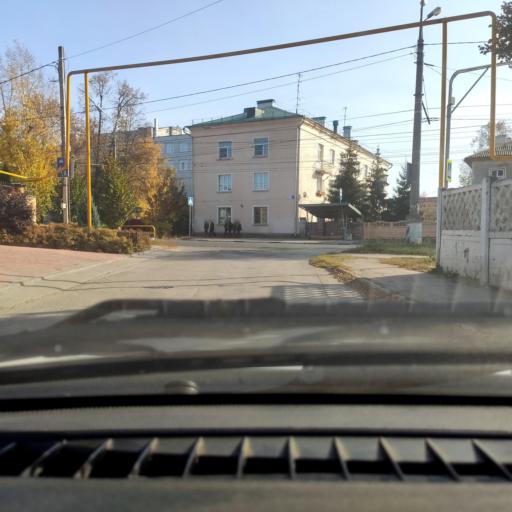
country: RU
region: Samara
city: Tol'yatti
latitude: 53.5062
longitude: 49.3956
